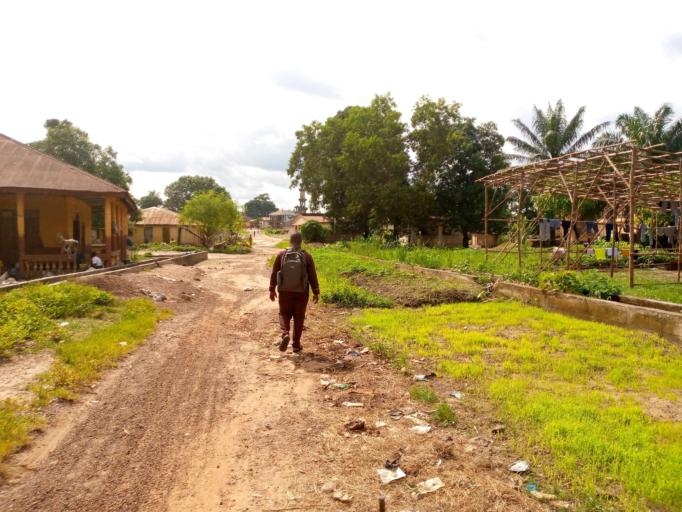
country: SL
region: Northern Province
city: Magburaka
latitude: 8.7235
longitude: -11.9470
